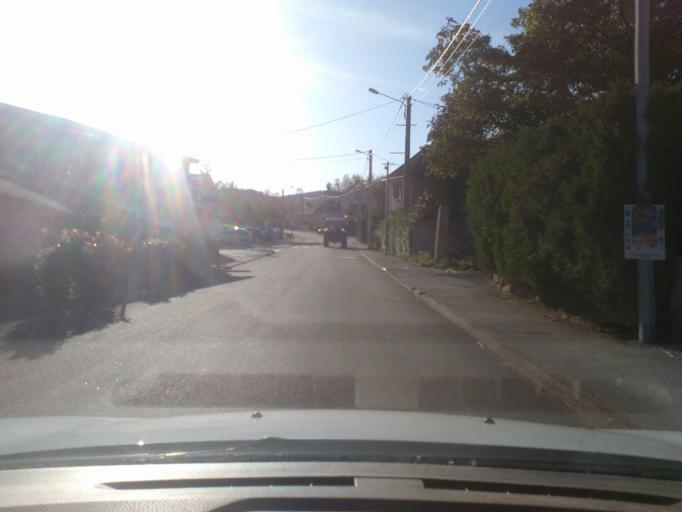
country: FR
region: Lorraine
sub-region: Departement des Vosges
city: Etival-Clairefontaine
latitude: 48.3122
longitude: 6.8276
